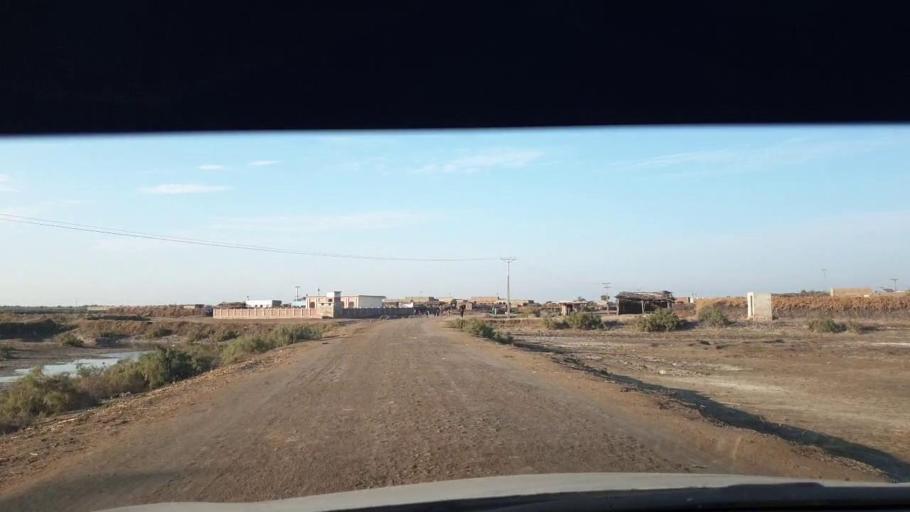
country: PK
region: Sindh
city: Berani
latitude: 25.8084
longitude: 68.9022
